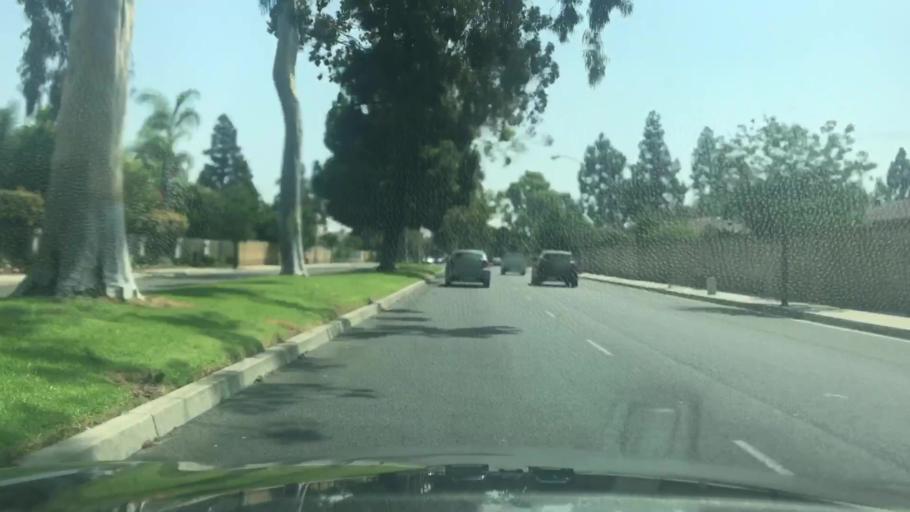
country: US
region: California
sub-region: Los Angeles County
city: Cerritos
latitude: 33.8585
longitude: -118.0676
